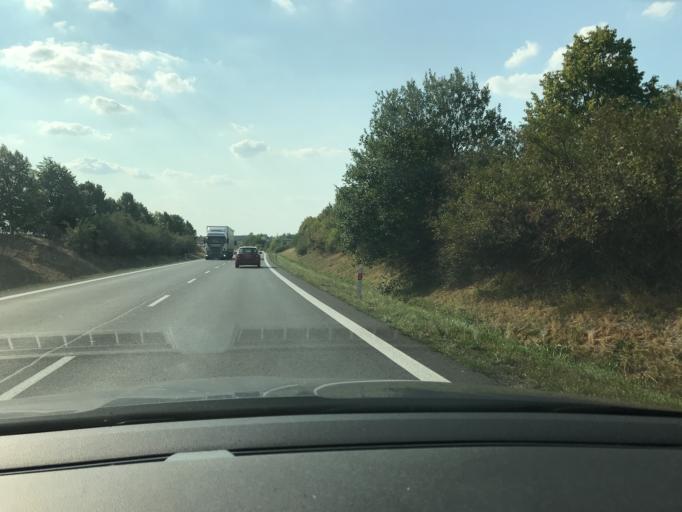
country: CZ
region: Central Bohemia
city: Velvary
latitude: 50.2712
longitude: 14.2339
